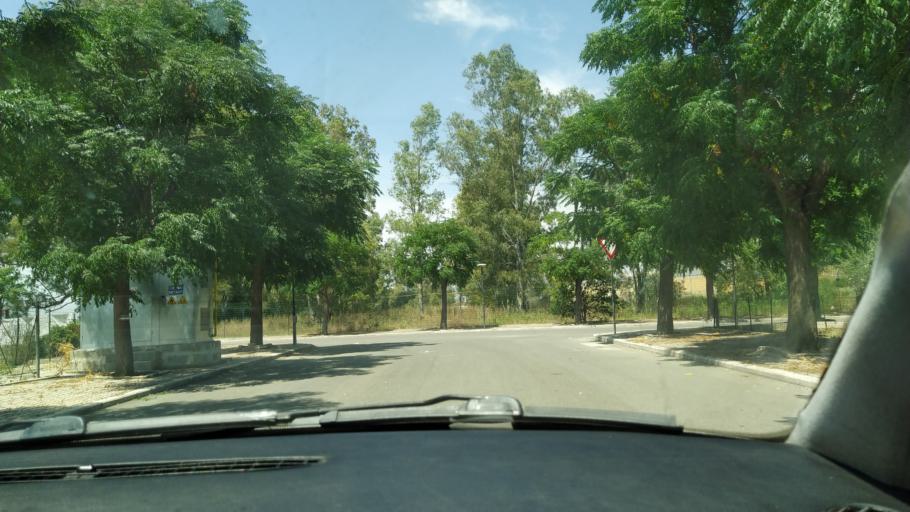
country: IT
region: Apulia
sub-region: Provincia di Taranto
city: Marina di Ginosa
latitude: 40.3719
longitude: 16.8088
